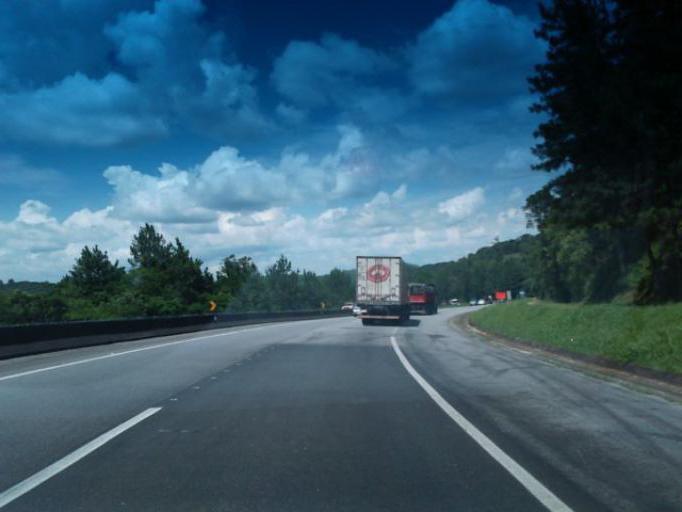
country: BR
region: Sao Paulo
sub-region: Juquitiba
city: Juquitiba
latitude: -23.9379
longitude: -47.0829
